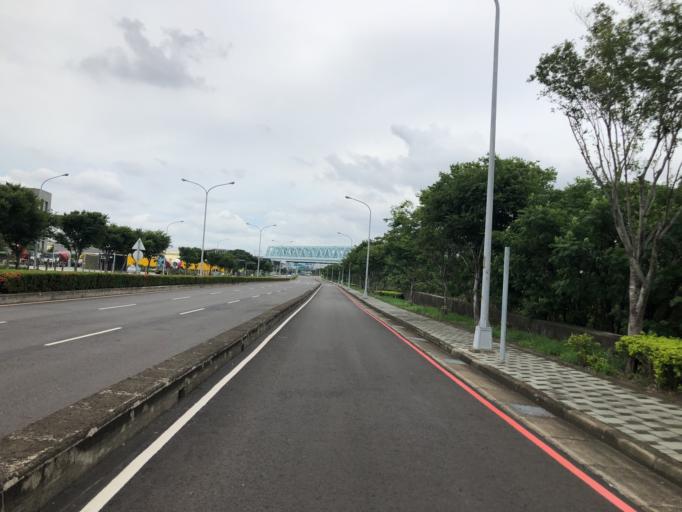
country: TW
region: Taiwan
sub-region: Changhua
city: Chang-hua
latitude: 24.1035
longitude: 120.6114
